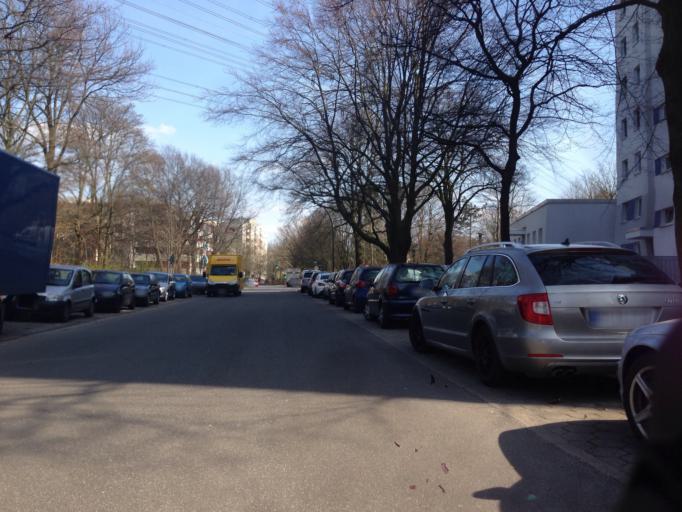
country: DE
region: Schleswig-Holstein
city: Barsbuettel
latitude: 53.5751
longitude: 10.1403
